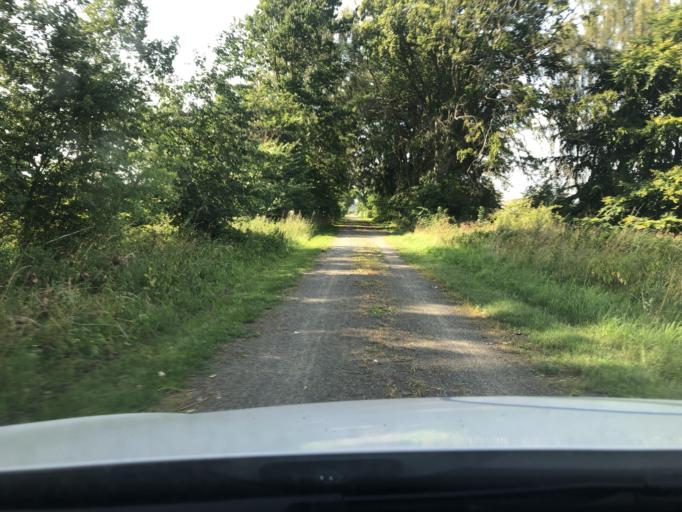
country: SE
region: Skane
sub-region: Kristianstads Kommun
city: Degeberga
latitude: 55.8166
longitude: 14.1257
